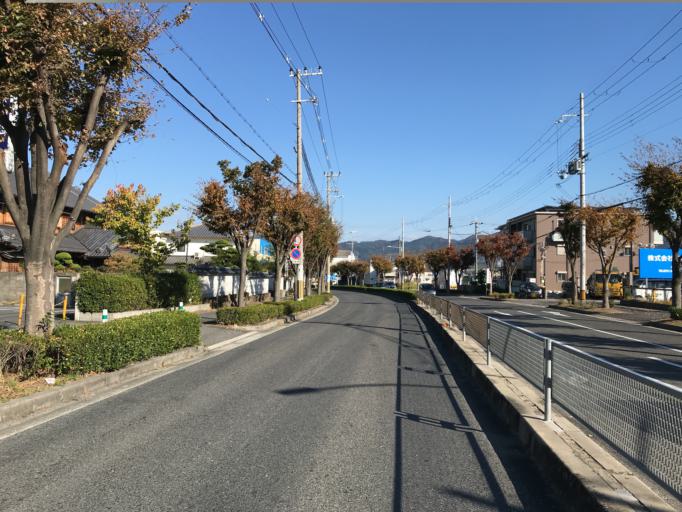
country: JP
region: Osaka
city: Tondabayashicho
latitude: 34.5107
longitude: 135.6081
